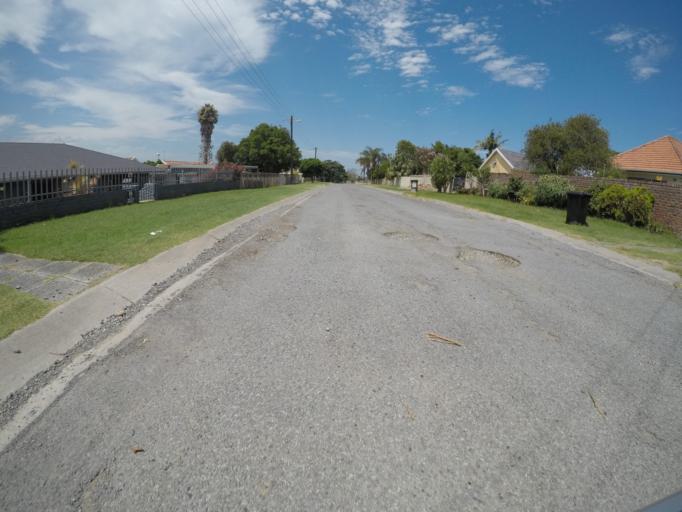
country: ZA
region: Eastern Cape
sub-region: Buffalo City Metropolitan Municipality
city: East London
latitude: -33.0312
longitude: 27.8650
